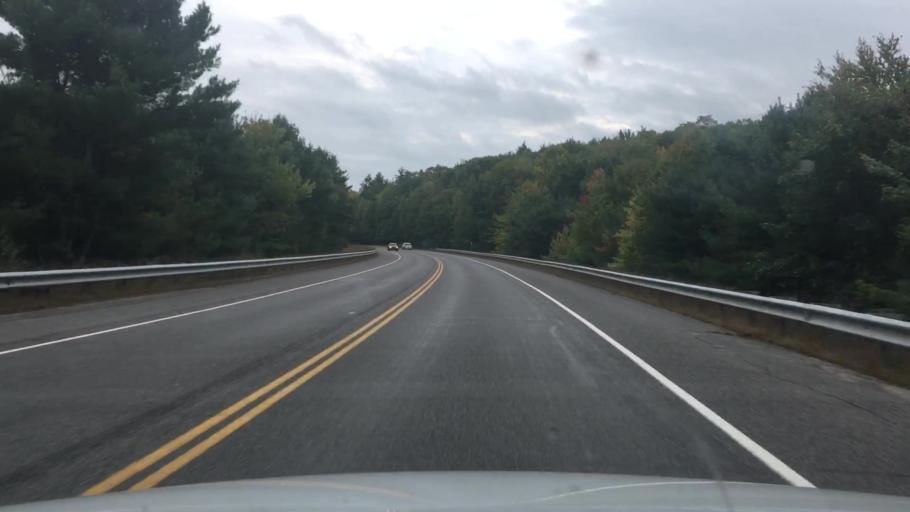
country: US
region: New Hampshire
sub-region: Carroll County
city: Wolfeboro
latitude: 43.5053
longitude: -71.2654
